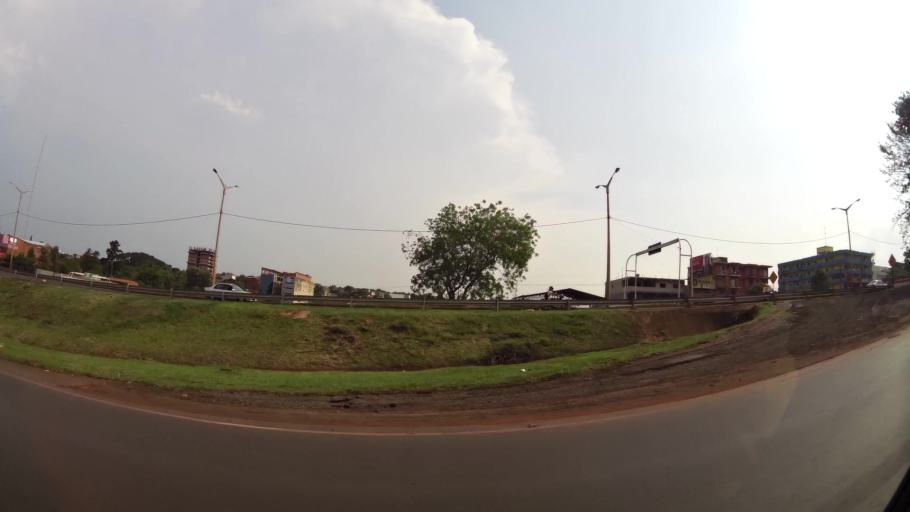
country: PY
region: Alto Parana
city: Ciudad del Este
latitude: -25.5039
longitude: -54.6519
